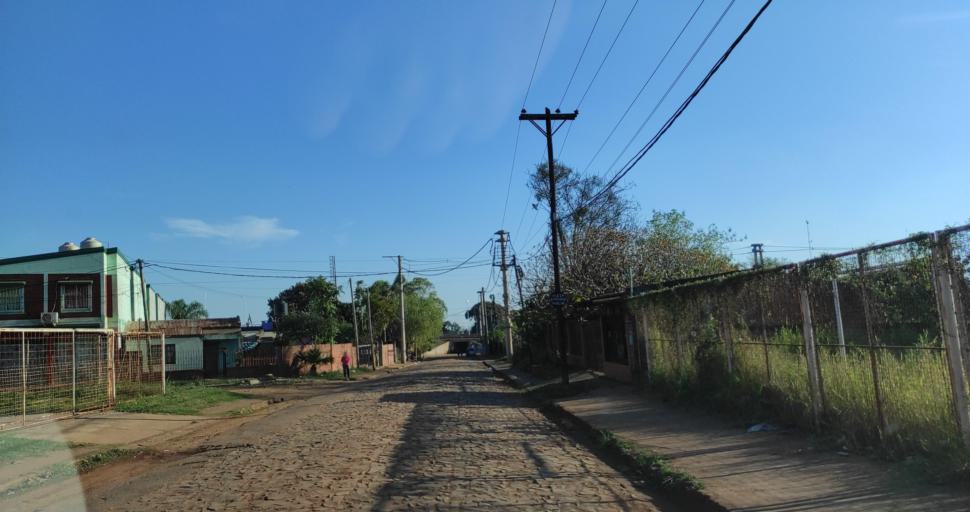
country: AR
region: Misiones
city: Garupa
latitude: -27.4510
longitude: -55.8640
